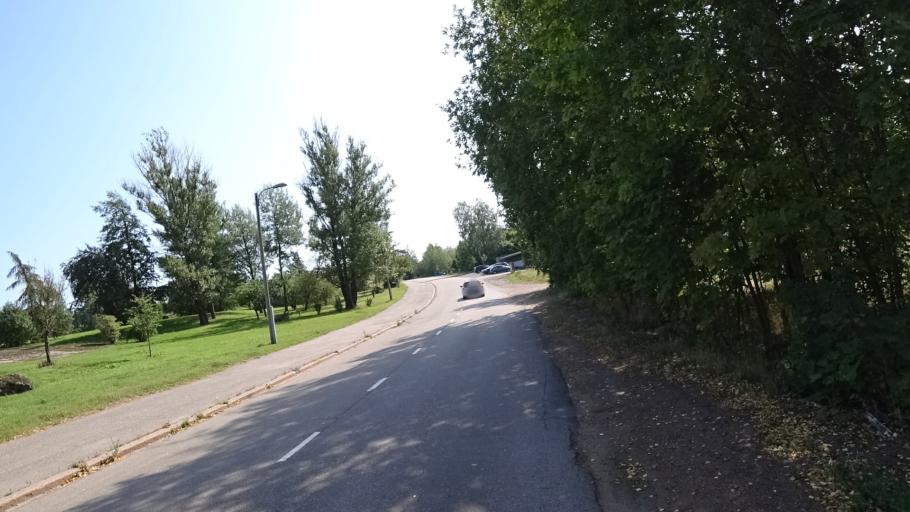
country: FI
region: Kymenlaakso
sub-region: Kotka-Hamina
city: Kotka
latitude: 60.4548
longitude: 26.9366
